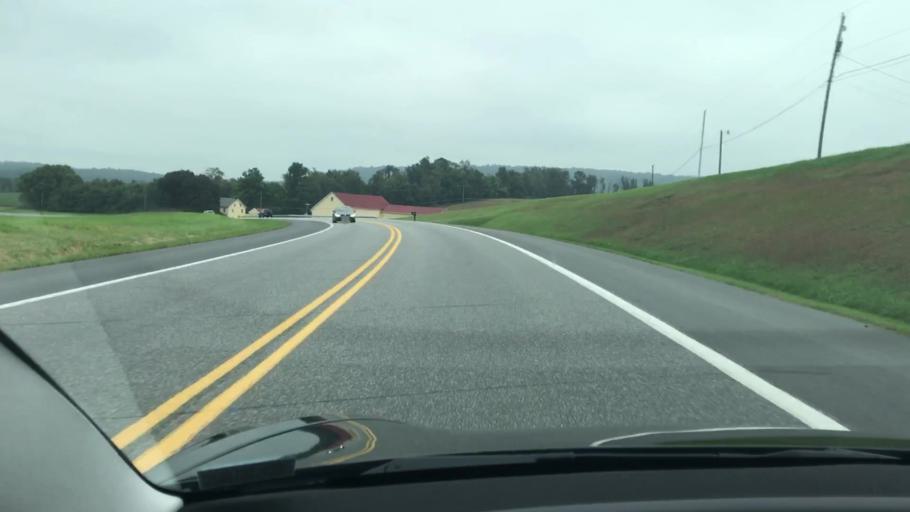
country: US
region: Pennsylvania
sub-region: Cumberland County
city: Lower Allen
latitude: 40.1497
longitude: -76.8835
